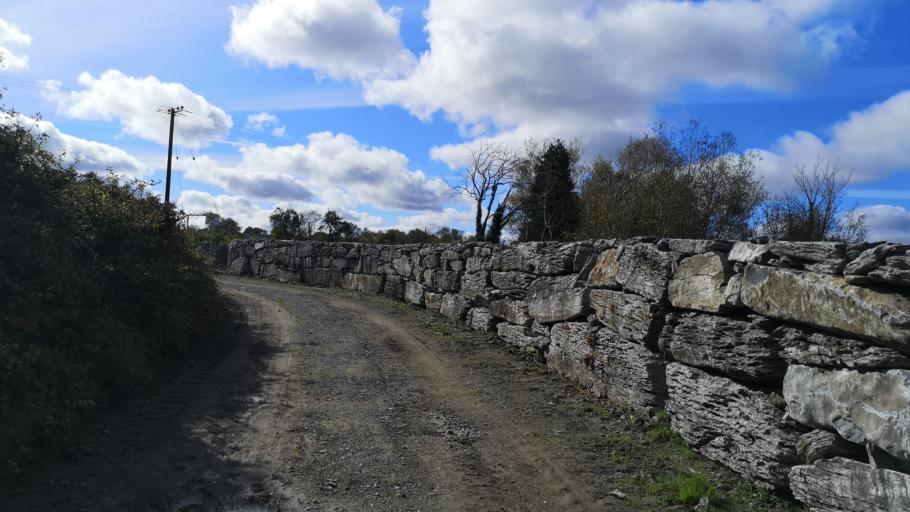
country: IE
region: Connaught
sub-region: County Galway
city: Gort
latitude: 53.0695
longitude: -8.8138
